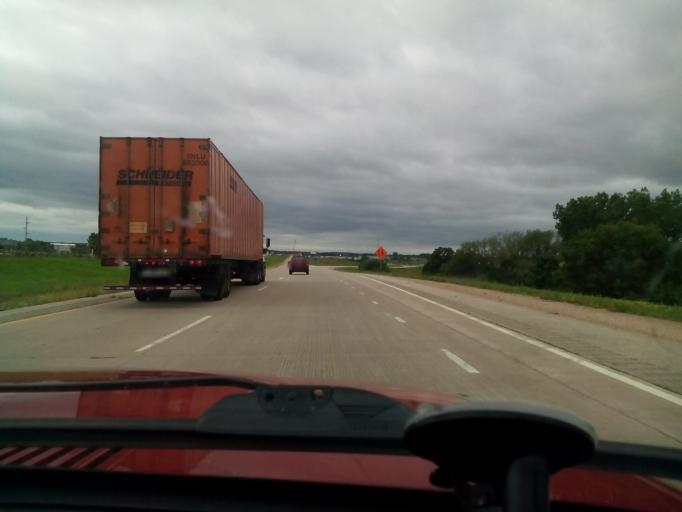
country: US
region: Wisconsin
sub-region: Columbia County
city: Columbus
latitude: 43.3520
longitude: -89.0285
